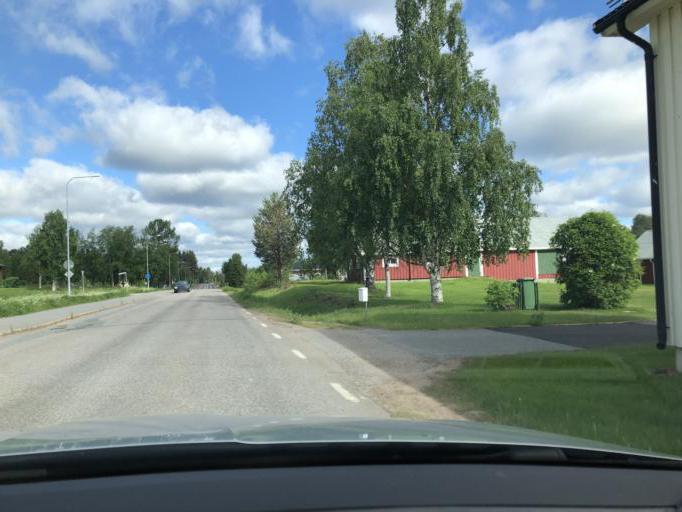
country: SE
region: Norrbotten
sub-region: Pajala Kommun
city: Pajala
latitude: 67.2203
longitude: 23.3503
